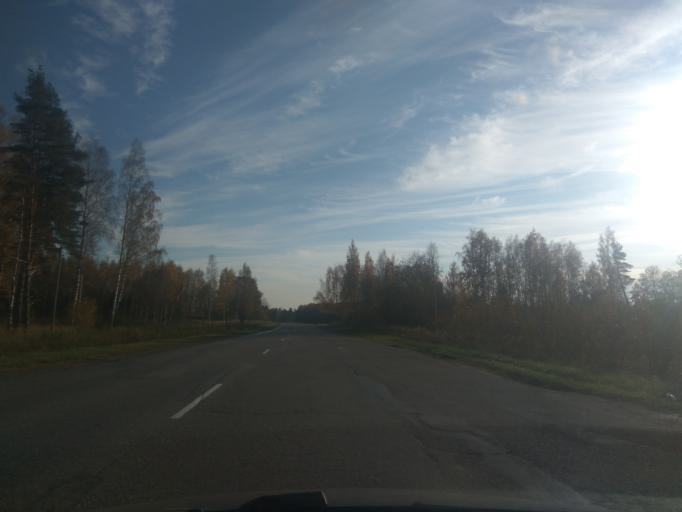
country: LV
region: Ventspils
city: Ventspils
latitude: 57.2952
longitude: 21.5632
